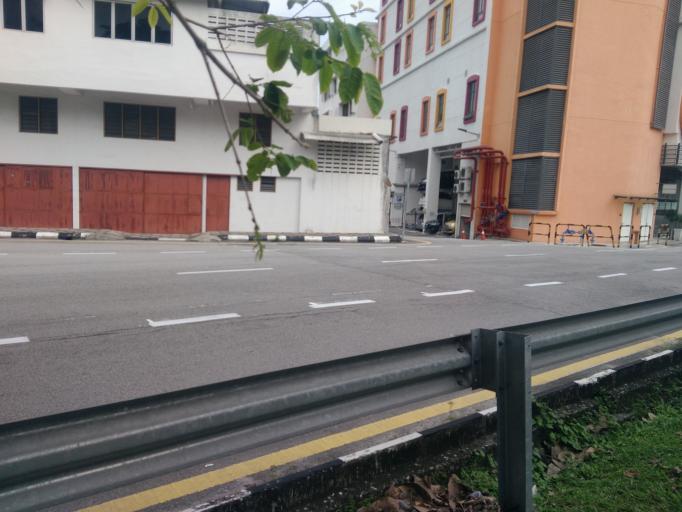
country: MY
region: Perak
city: Ipoh
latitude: 4.5986
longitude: 101.0787
